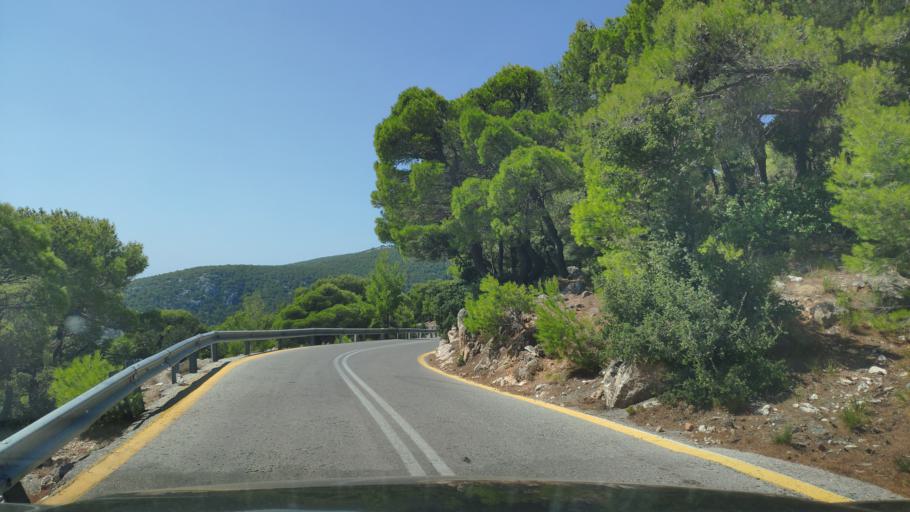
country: GR
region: Attica
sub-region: Nomarchia Anatolikis Attikis
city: Thrakomakedones
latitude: 38.1395
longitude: 23.7228
